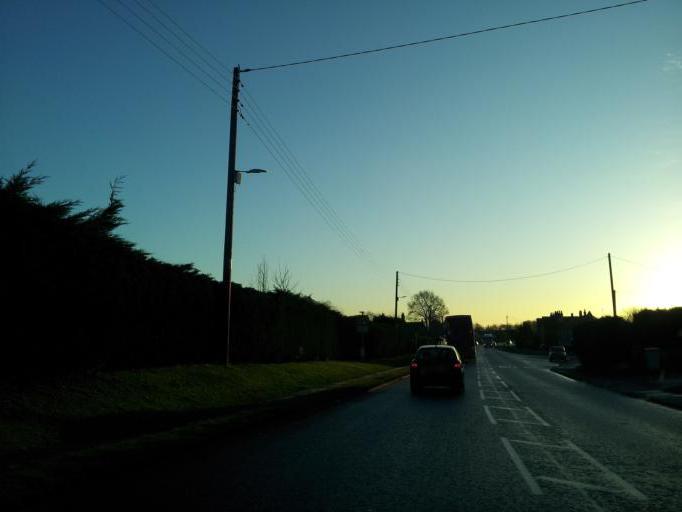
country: GB
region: England
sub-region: Lincolnshire
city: Market Rasen
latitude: 53.2865
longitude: -0.2964
